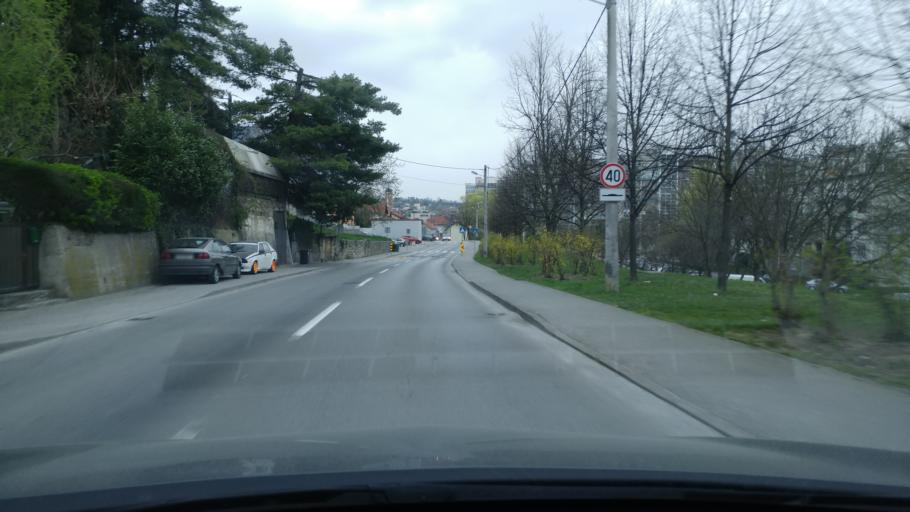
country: HR
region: Grad Zagreb
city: Stenjevec
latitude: 45.8193
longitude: 15.8747
